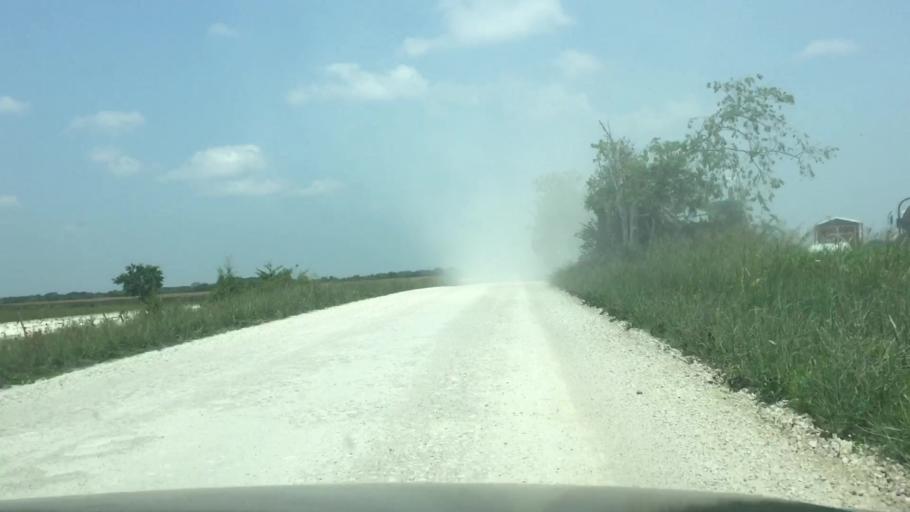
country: US
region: Kansas
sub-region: Allen County
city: Humboldt
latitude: 37.8326
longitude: -95.4094
